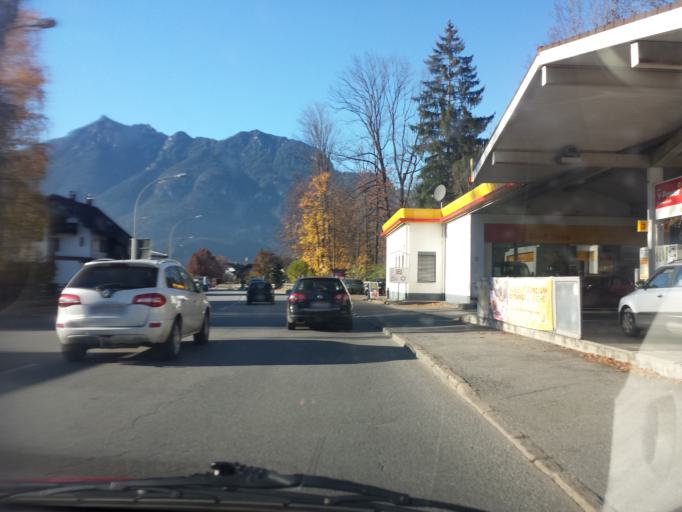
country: DE
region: Bavaria
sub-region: Upper Bavaria
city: Garmisch-Partenkirchen
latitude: 47.4899
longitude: 11.1129
